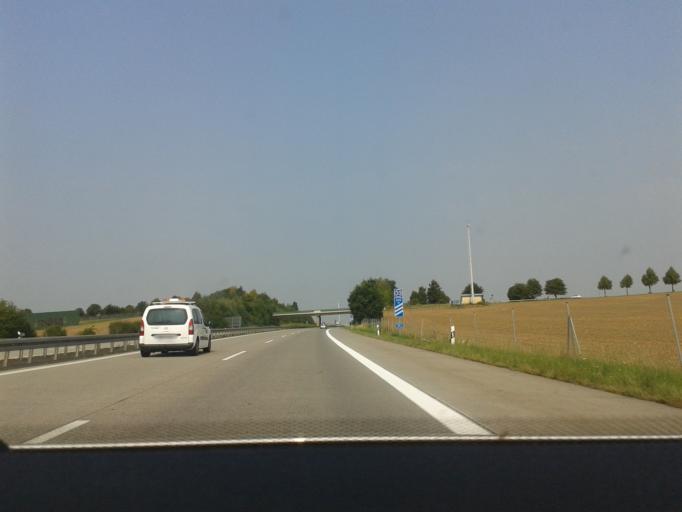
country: DE
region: Saxony
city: Bockelwitz
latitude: 51.1979
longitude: 12.9725
